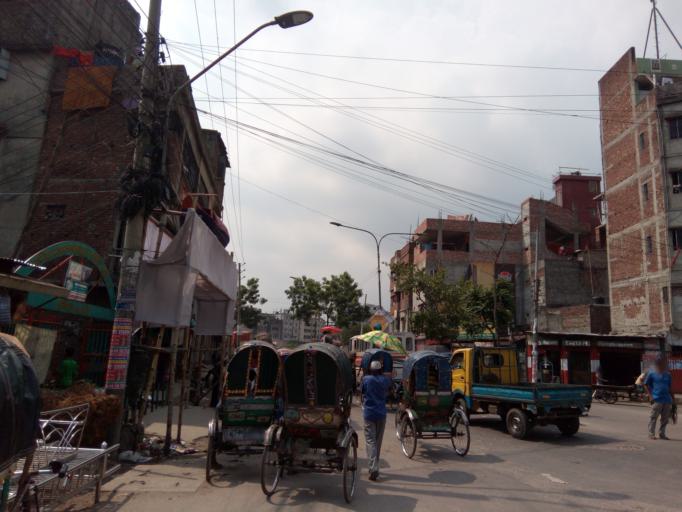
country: BD
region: Dhaka
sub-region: Dhaka
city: Dhaka
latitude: 23.7084
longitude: 90.4200
